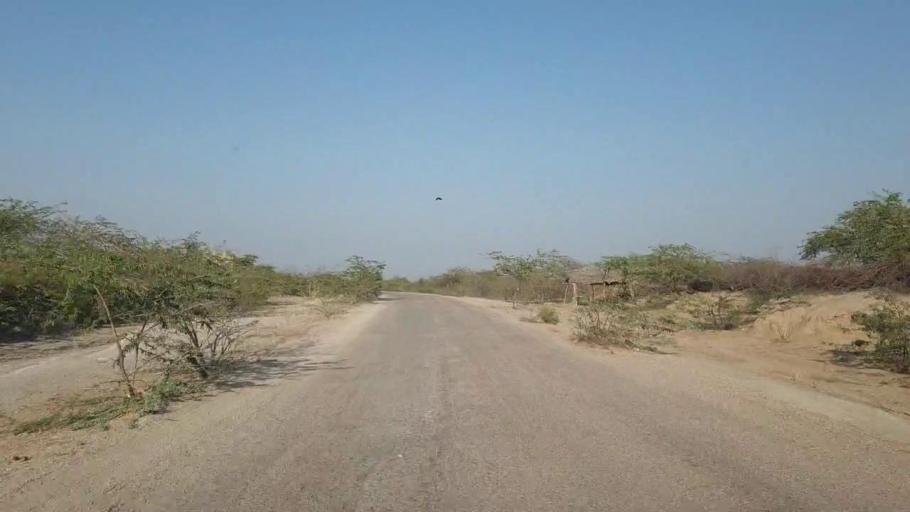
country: PK
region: Sindh
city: Chor
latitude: 25.5428
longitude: 69.7808
